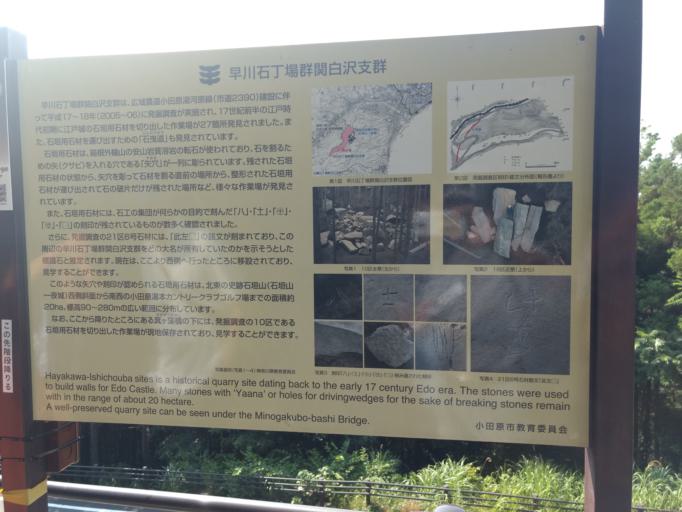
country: JP
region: Kanagawa
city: Odawara
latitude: 35.2316
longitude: 139.1228
